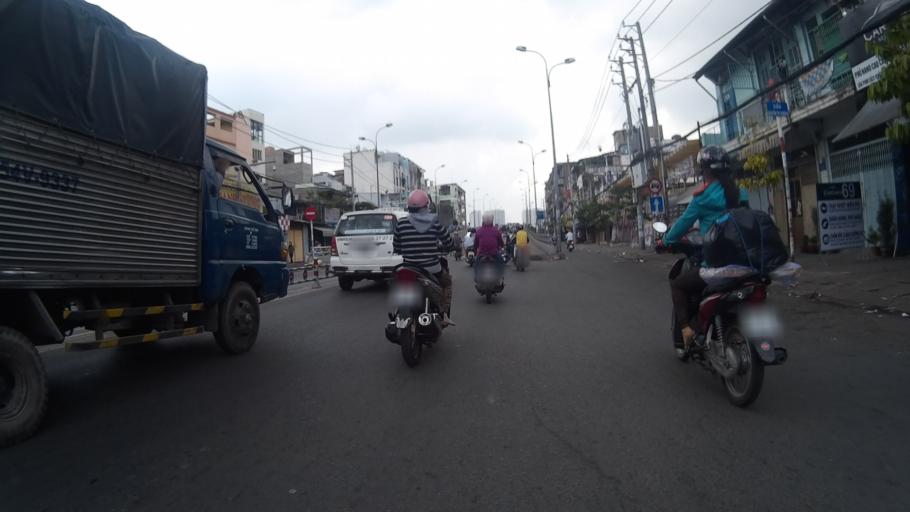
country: VN
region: Ho Chi Minh City
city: Quan Nam
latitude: 10.7525
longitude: 106.6693
